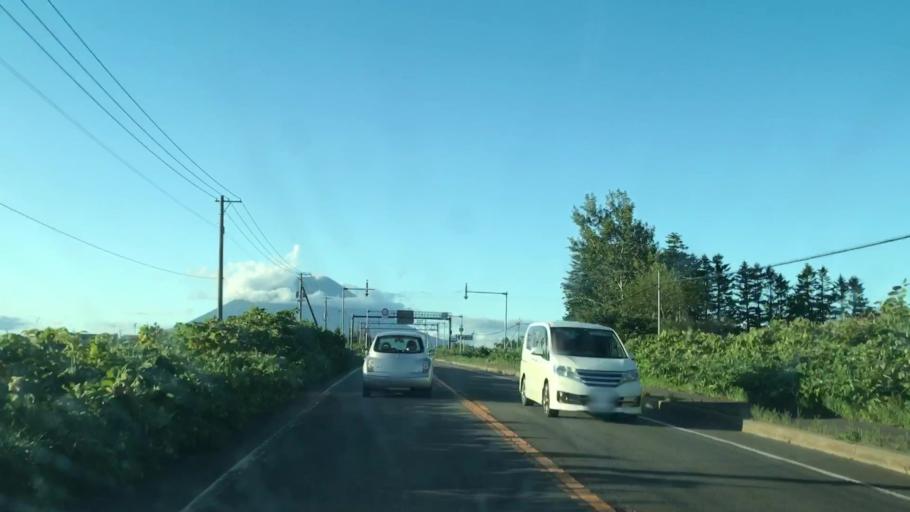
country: JP
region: Hokkaido
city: Niseko Town
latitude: 42.6708
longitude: 140.8424
